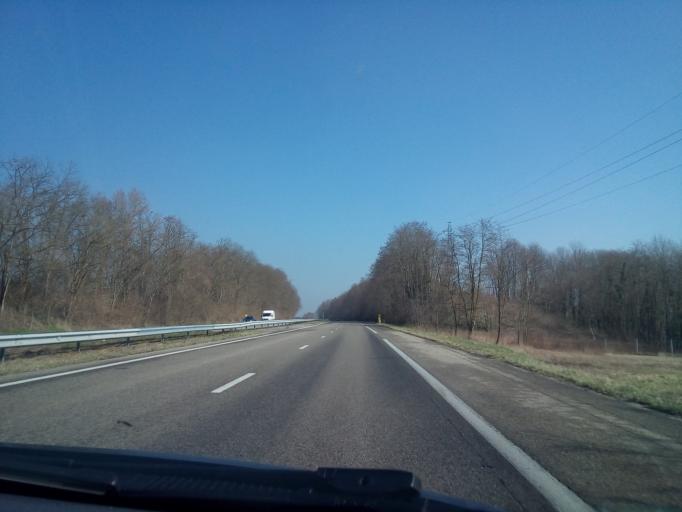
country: DE
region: Rheinland-Pfalz
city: Scheibenhardt
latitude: 48.9512
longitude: 8.1411
